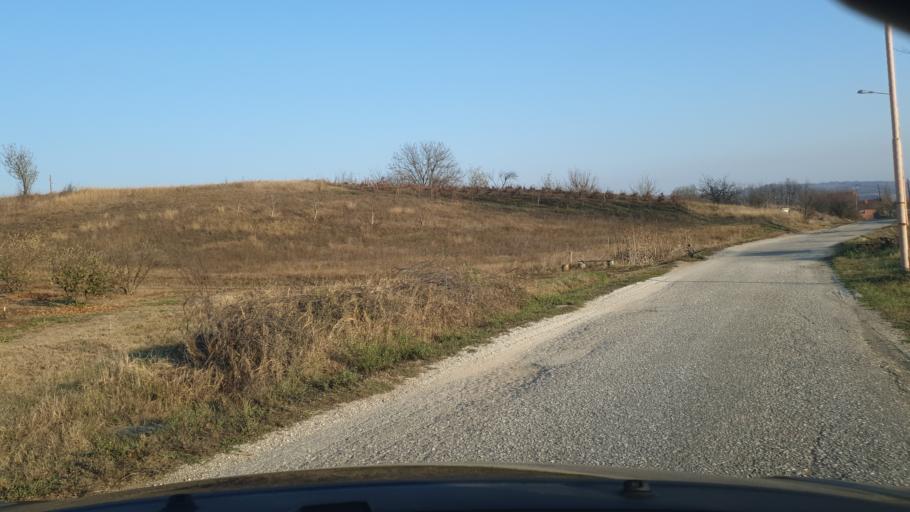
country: RS
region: Central Serbia
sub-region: Zajecarski Okrug
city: Zajecar
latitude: 44.0890
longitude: 22.3491
